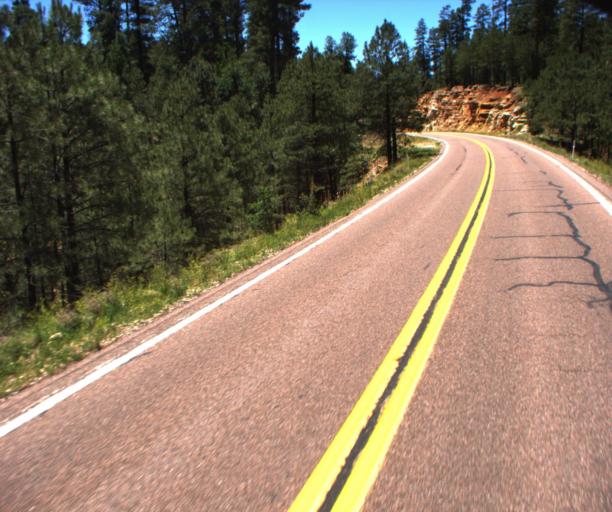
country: US
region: Arizona
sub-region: Gila County
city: Pine
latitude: 34.5085
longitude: -111.3590
